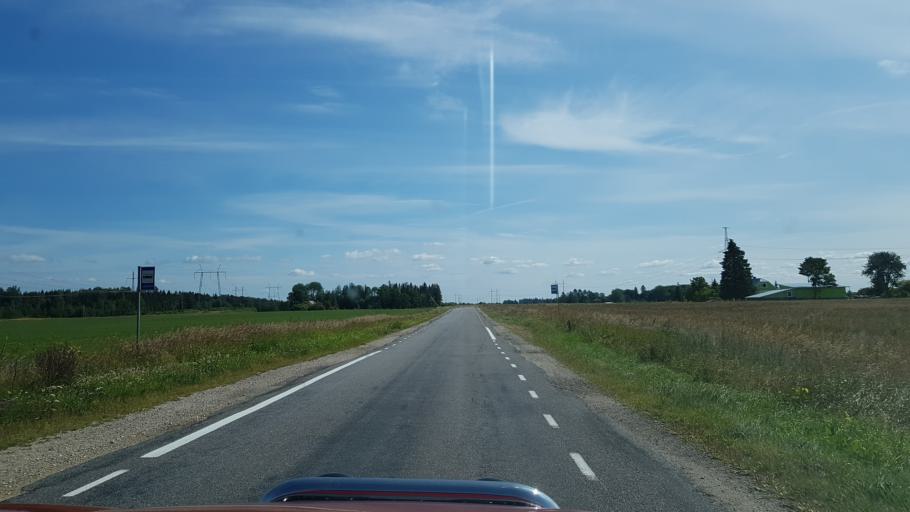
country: EE
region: Laeaene-Virumaa
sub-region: Tapa vald
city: Tapa
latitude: 59.1872
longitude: 25.8631
